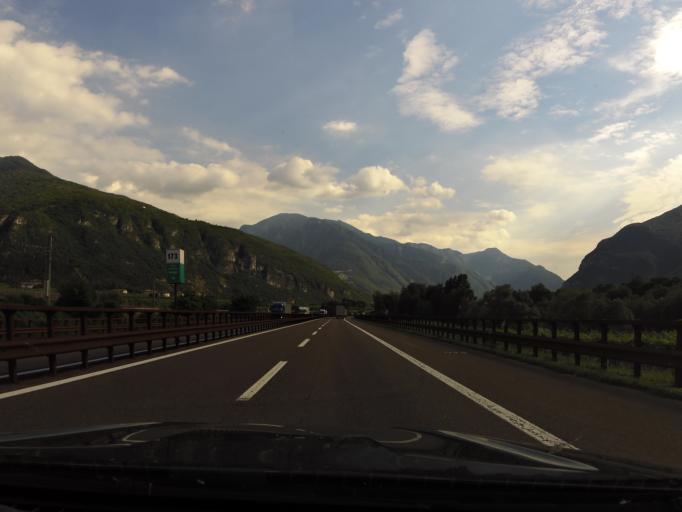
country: IT
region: Trentino-Alto Adige
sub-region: Provincia di Trento
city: Ala
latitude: 45.7911
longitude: 11.0204
